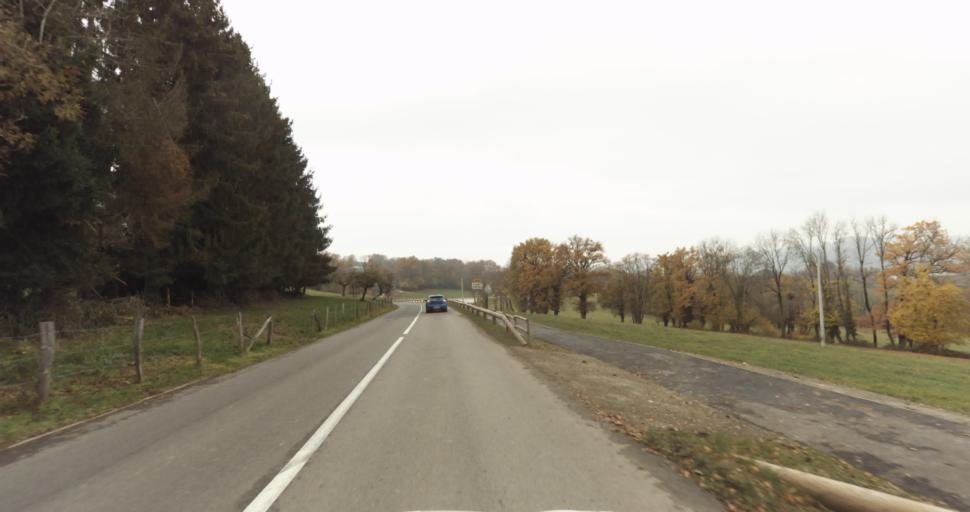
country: FR
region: Rhone-Alpes
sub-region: Departement de la Haute-Savoie
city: Alby-sur-Cheran
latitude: 45.7990
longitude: 6.0126
